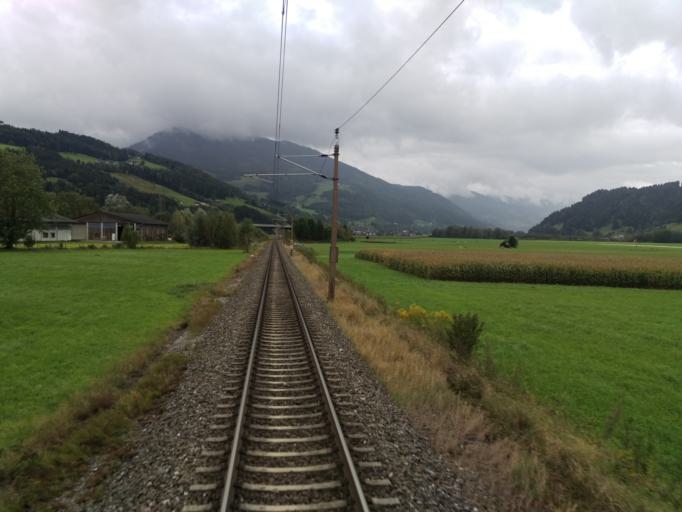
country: AT
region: Styria
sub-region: Politischer Bezirk Liezen
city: Niederoblarn
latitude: 47.4807
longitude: 14.0136
